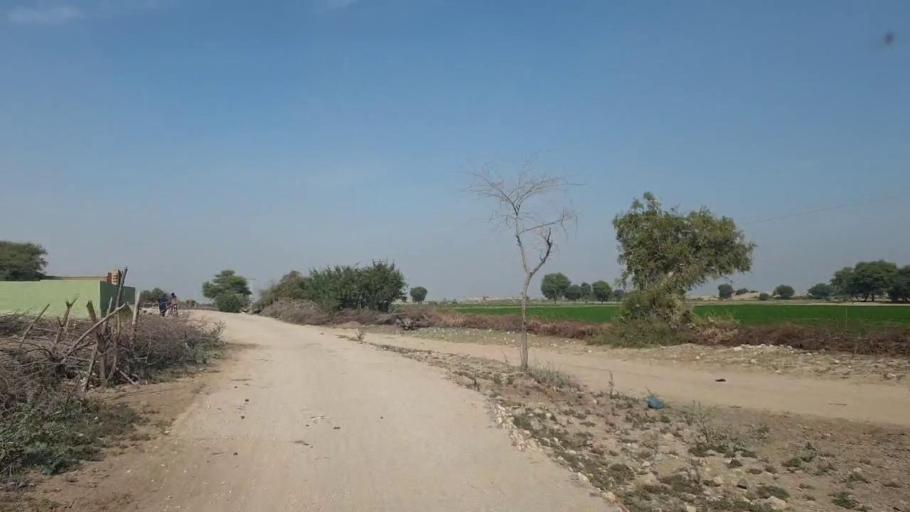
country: PK
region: Sindh
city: Hala
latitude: 25.7593
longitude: 68.2957
